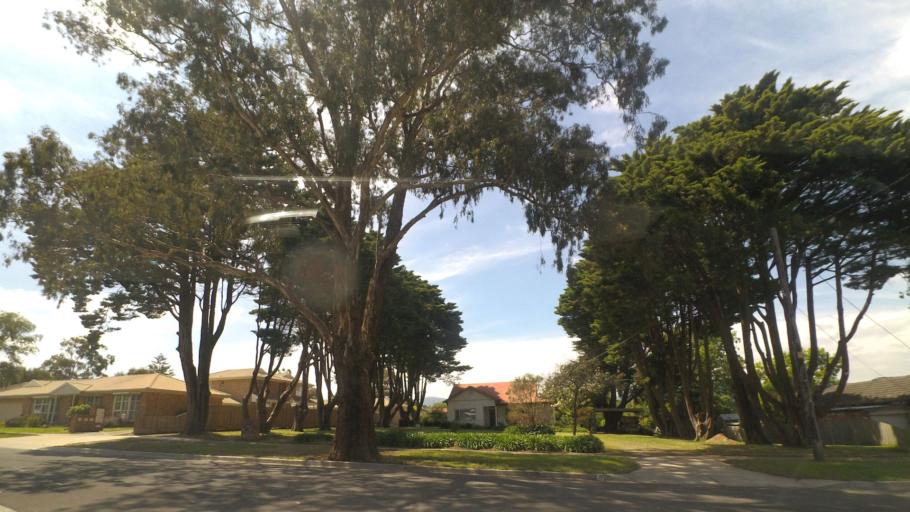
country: AU
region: Victoria
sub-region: Knox
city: Bayswater
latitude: -37.8461
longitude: 145.2604
